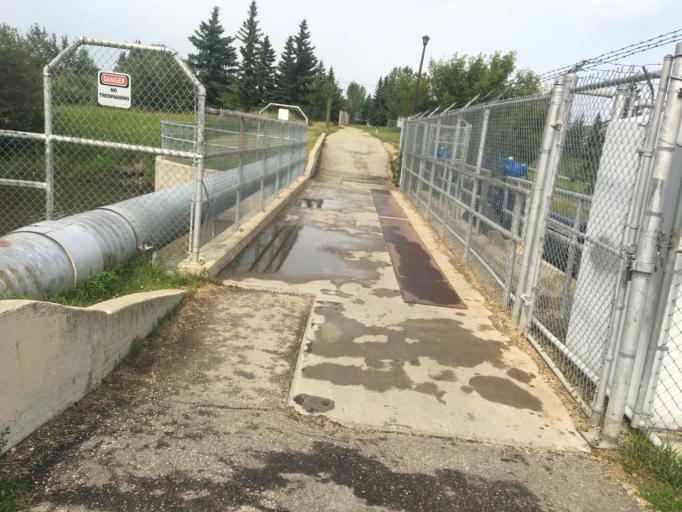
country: CA
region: Alberta
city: Grande Prairie
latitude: 55.1758
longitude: -118.8086
